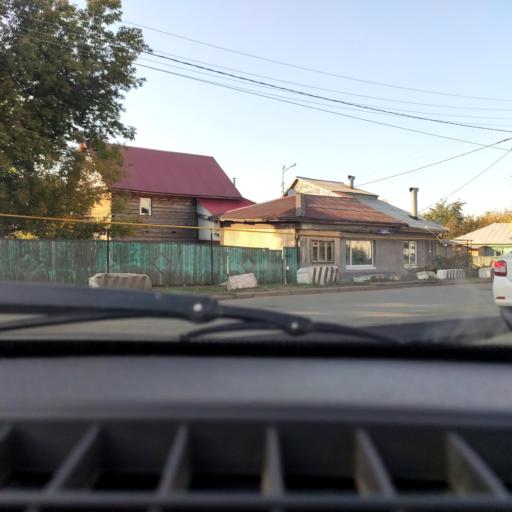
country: RU
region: Bashkortostan
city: Ufa
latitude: 54.7474
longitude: 55.9786
